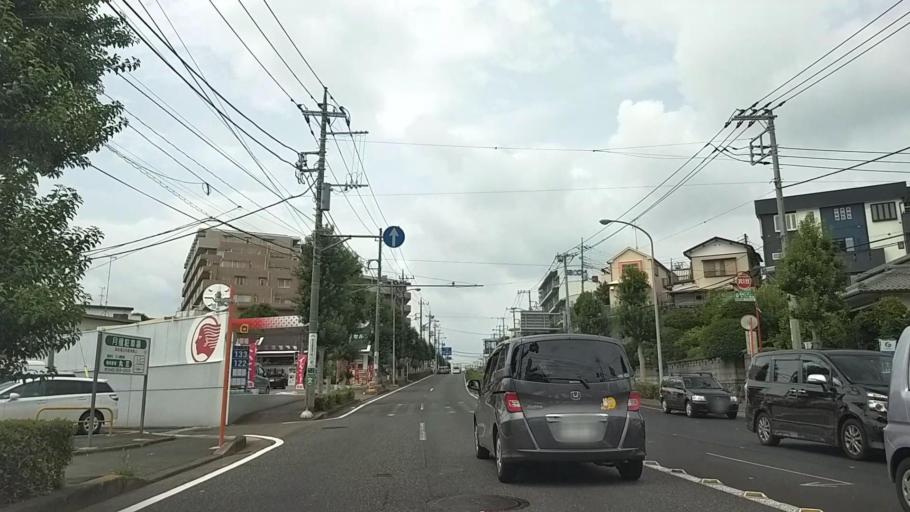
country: JP
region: Kanagawa
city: Minami-rinkan
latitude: 35.4681
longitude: 139.4935
